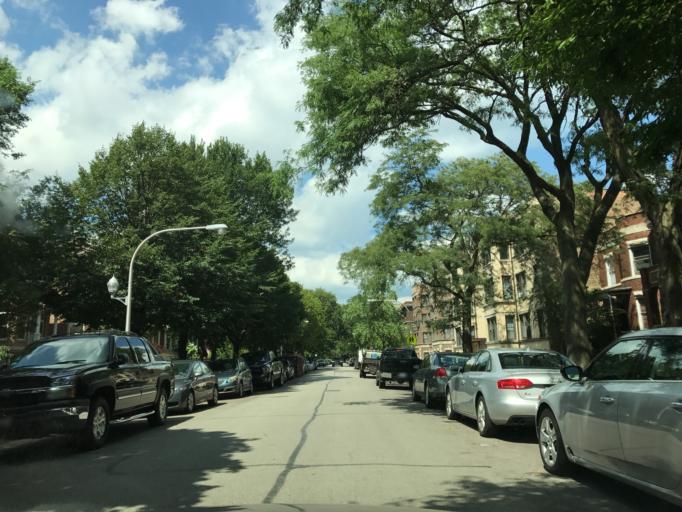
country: US
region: Illinois
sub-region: Cook County
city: Chicago
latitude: 41.7967
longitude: -87.6012
